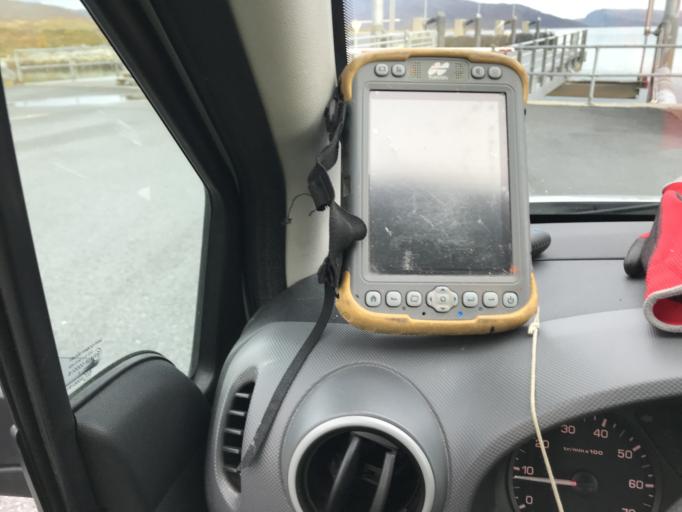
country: NO
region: Troms
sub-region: Tromso
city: Tromso
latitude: 70.0774
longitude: 18.9829
